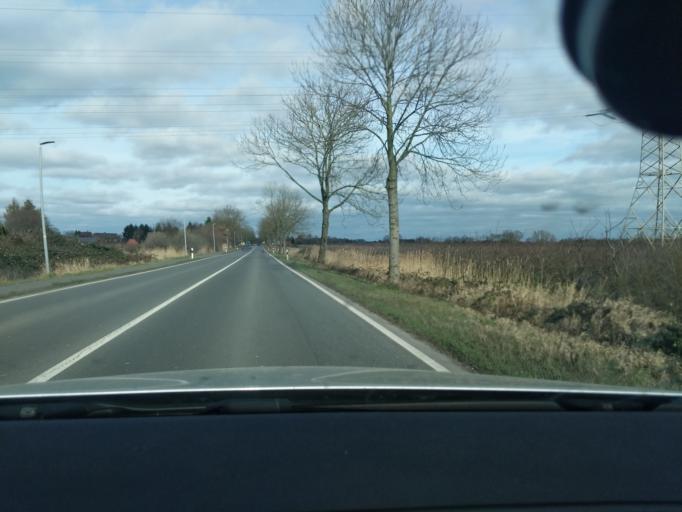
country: DE
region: Lower Saxony
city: Stade
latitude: 53.6587
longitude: 9.4764
